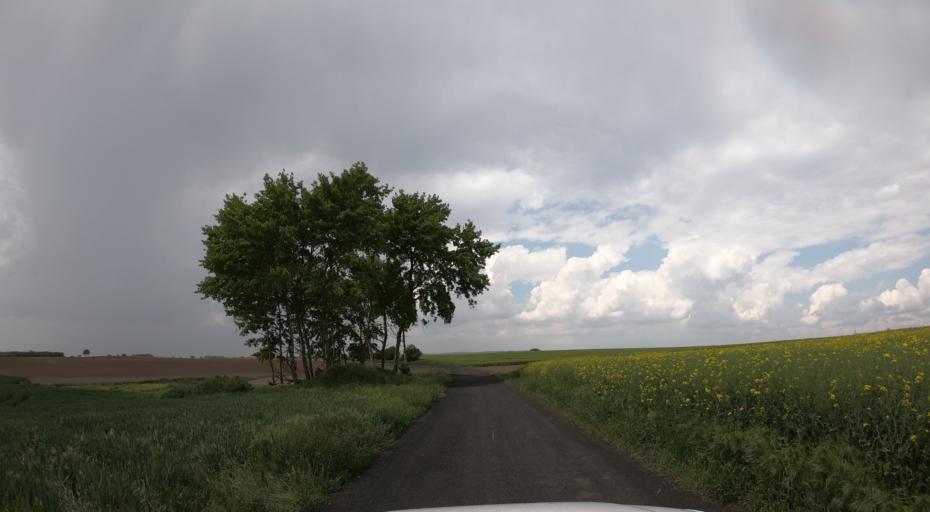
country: PL
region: West Pomeranian Voivodeship
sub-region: Powiat pyrzycki
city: Bielice
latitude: 53.2636
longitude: 14.6967
